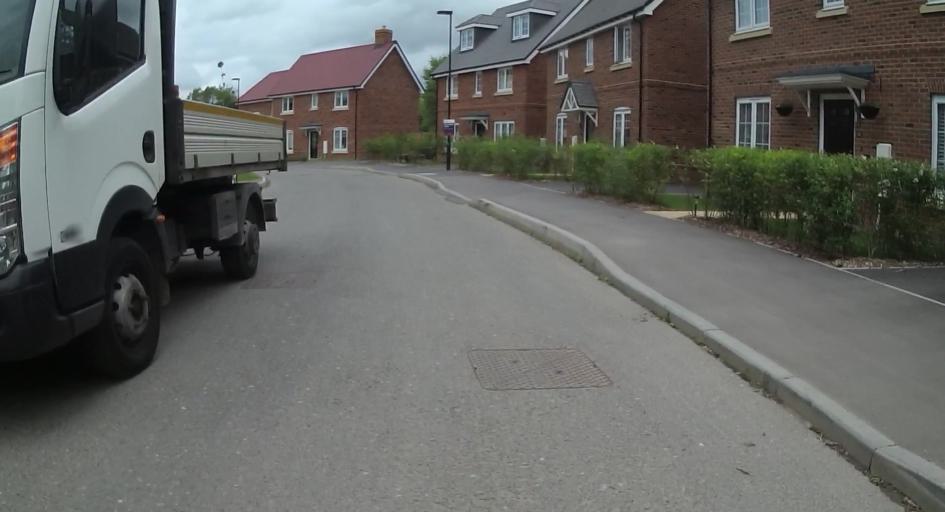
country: GB
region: England
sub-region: Surrey
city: Farnham
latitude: 51.2148
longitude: -0.8107
